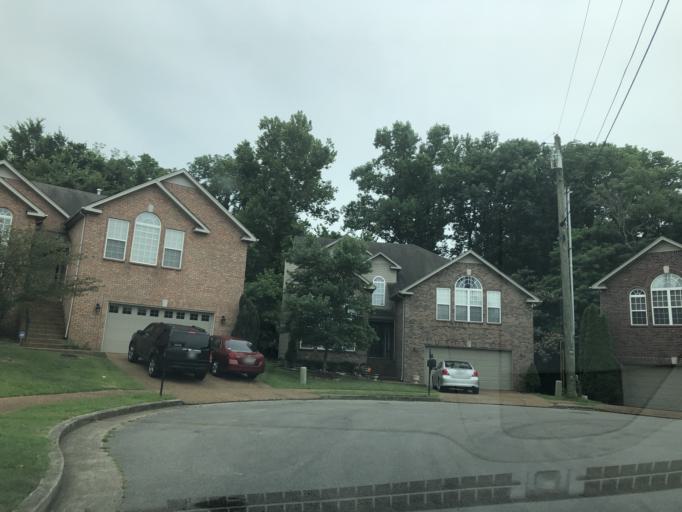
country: US
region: Tennessee
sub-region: Williamson County
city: Nolensville
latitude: 36.0302
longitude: -86.6797
